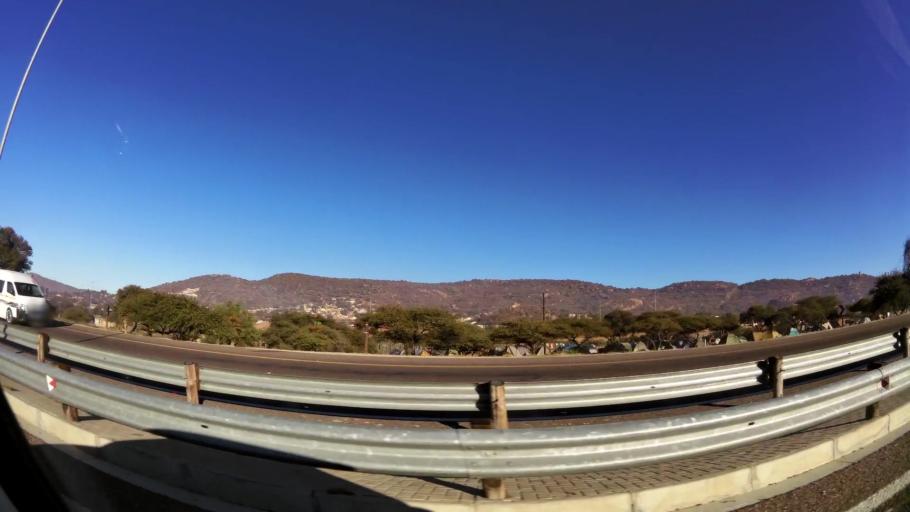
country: ZA
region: Limpopo
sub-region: Capricorn District Municipality
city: Mankoeng
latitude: -23.9384
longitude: 29.7948
